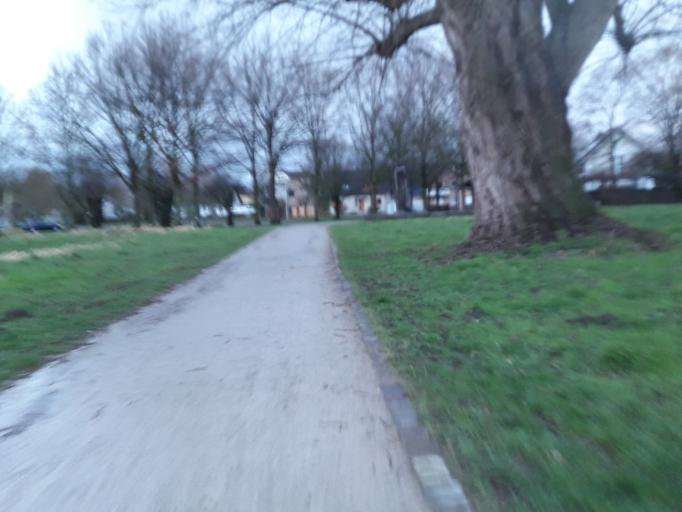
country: DE
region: North Rhine-Westphalia
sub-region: Regierungsbezirk Detmold
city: Paderborn
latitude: 51.7458
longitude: 8.7074
